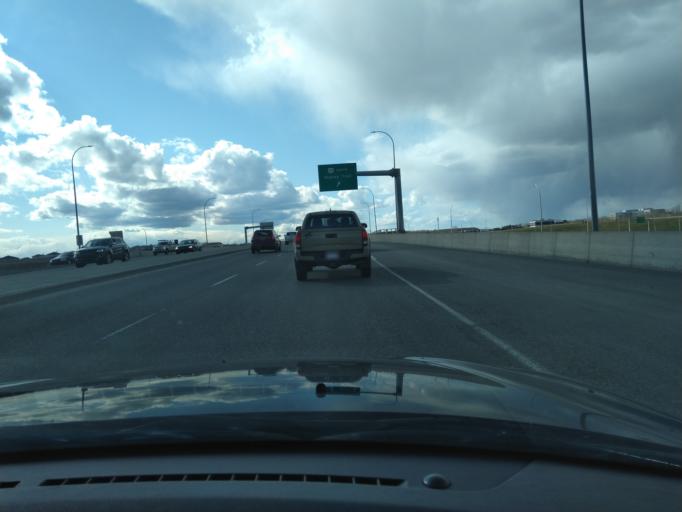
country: CA
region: Alberta
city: Calgary
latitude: 51.1441
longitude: -114.2016
